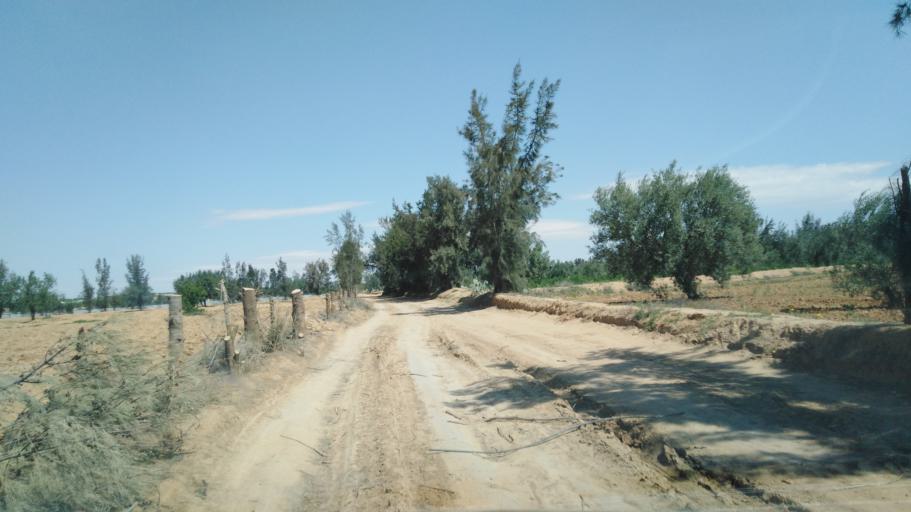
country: TN
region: Safaqis
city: Sfax
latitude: 34.7654
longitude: 10.5282
